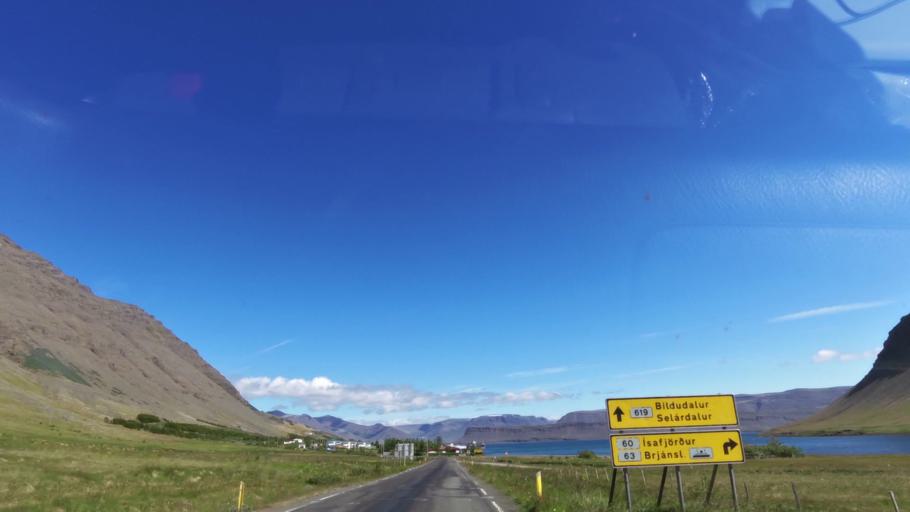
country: IS
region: Westfjords
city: Isafjoerdur
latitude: 65.6755
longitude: -23.6159
